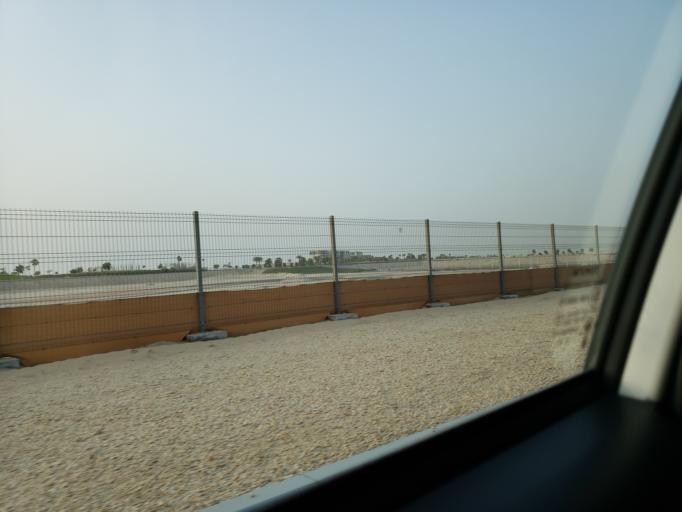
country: AE
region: Ajman
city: Ajman
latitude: 25.4297
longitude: 55.4621
